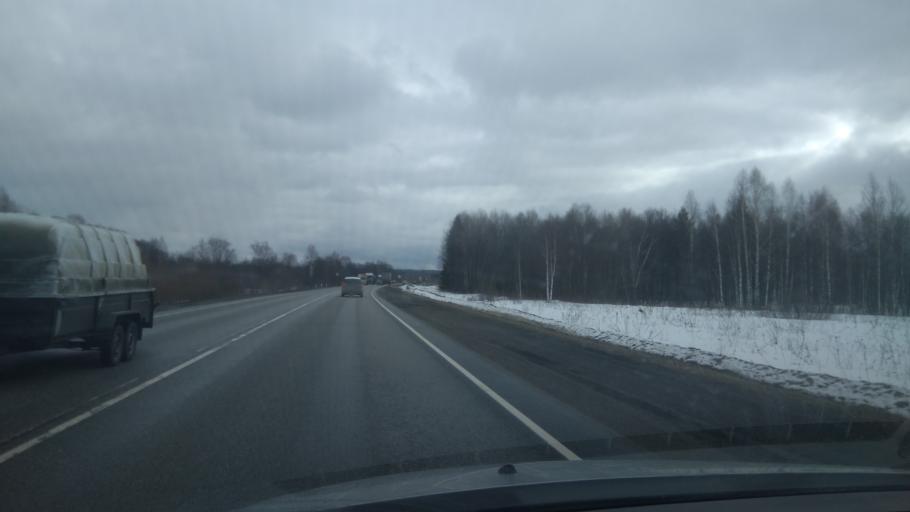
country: RU
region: Sverdlovsk
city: Ufimskiy
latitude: 56.7698
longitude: 58.1238
